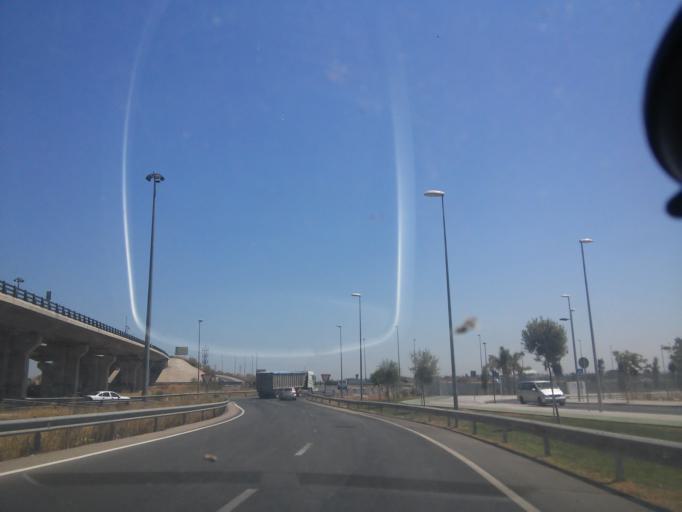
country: ES
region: Andalusia
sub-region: Provincia de Sevilla
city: La Algaba
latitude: 37.4348
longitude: -5.9735
